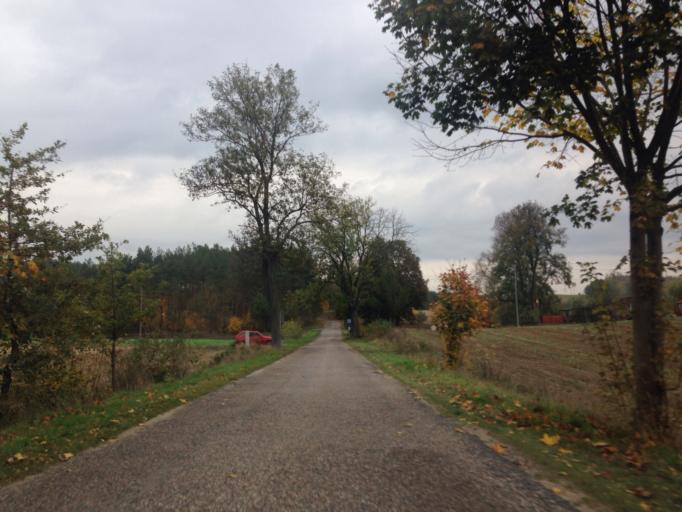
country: PL
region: Kujawsko-Pomorskie
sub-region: Powiat brodnicki
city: Gorzno
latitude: 53.2673
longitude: 19.6903
